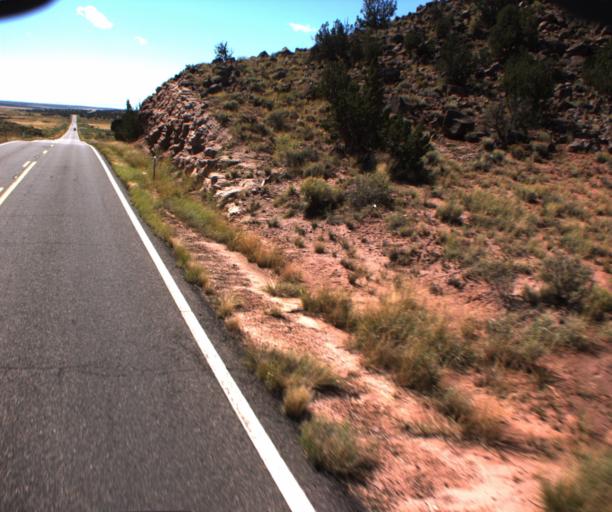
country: US
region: Arizona
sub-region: Apache County
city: Saint Johns
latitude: 34.7501
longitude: -109.2458
